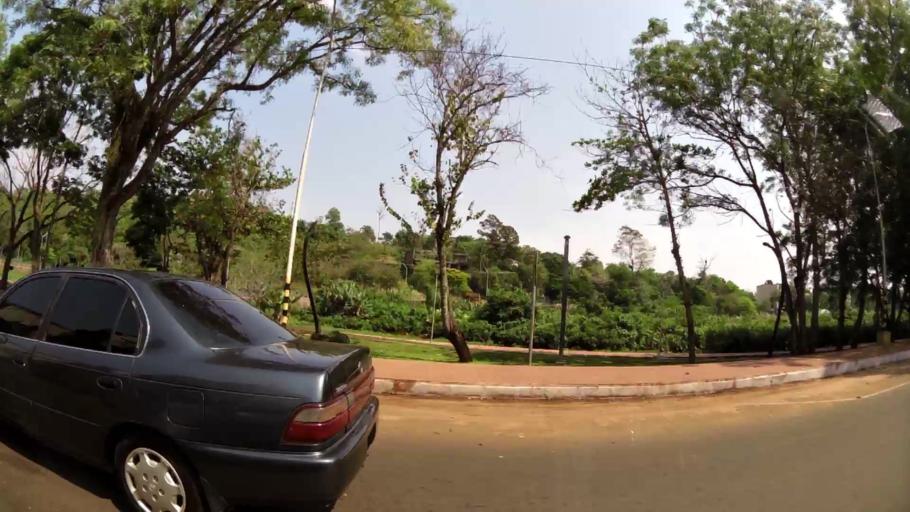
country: PY
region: Alto Parana
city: Presidente Franco
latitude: -25.5210
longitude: -54.6238
